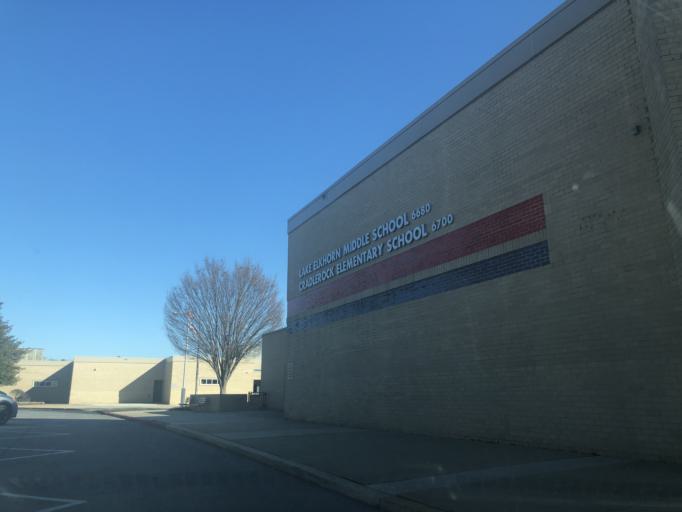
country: US
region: Maryland
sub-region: Howard County
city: Riverside
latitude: 39.1916
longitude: -76.8440
